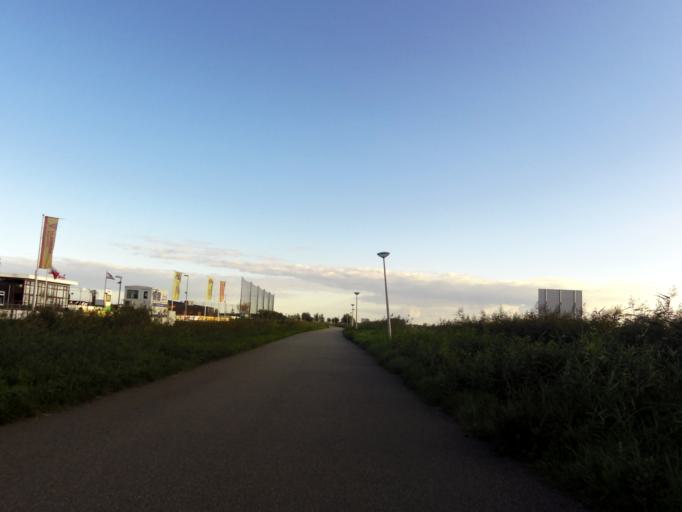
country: NL
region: South Holland
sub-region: Gemeente Alphen aan den Rijn
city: Alphen aan den Rijn
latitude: 52.1190
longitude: 4.6331
